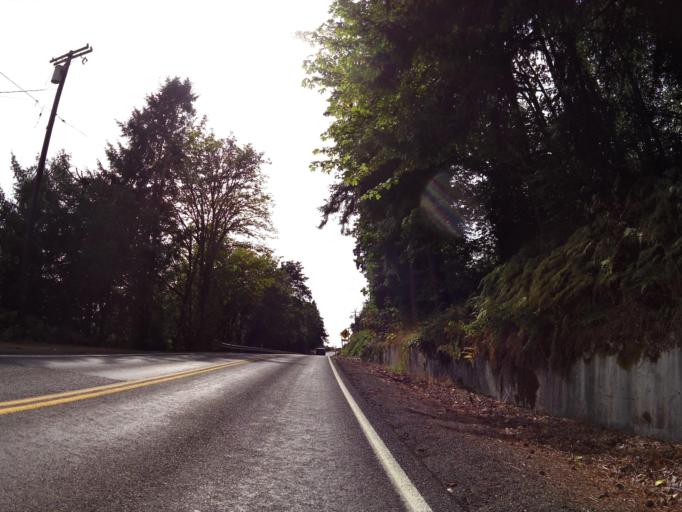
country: US
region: Washington
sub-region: Lewis County
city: Chehalis
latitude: 46.6297
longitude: -122.9684
